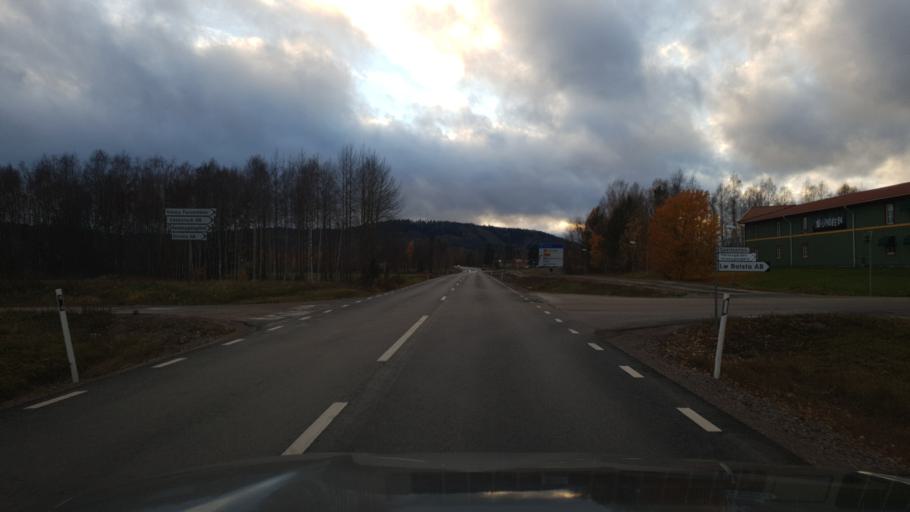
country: SE
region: Gaevleborg
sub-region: Ovanakers Kommun
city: Edsbyn
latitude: 61.3701
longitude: 15.8267
